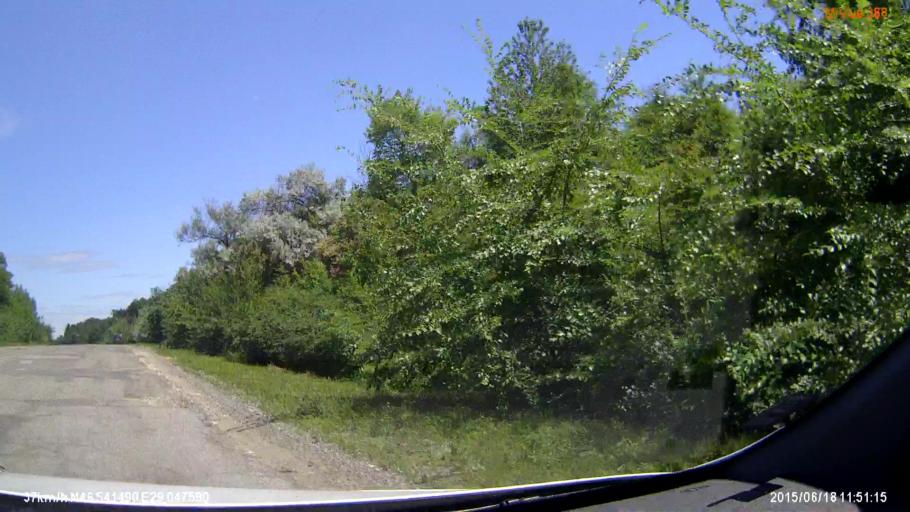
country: MD
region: Basarabeasca
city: Basarabeasca
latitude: 46.5414
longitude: 29.0474
